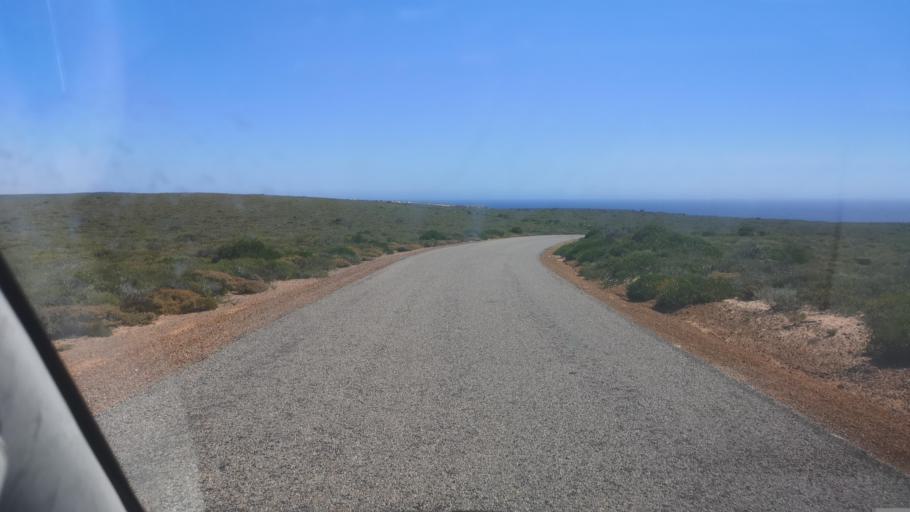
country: AU
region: Western Australia
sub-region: Northampton Shire
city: Kalbarri
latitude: -27.8263
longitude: 114.1166
